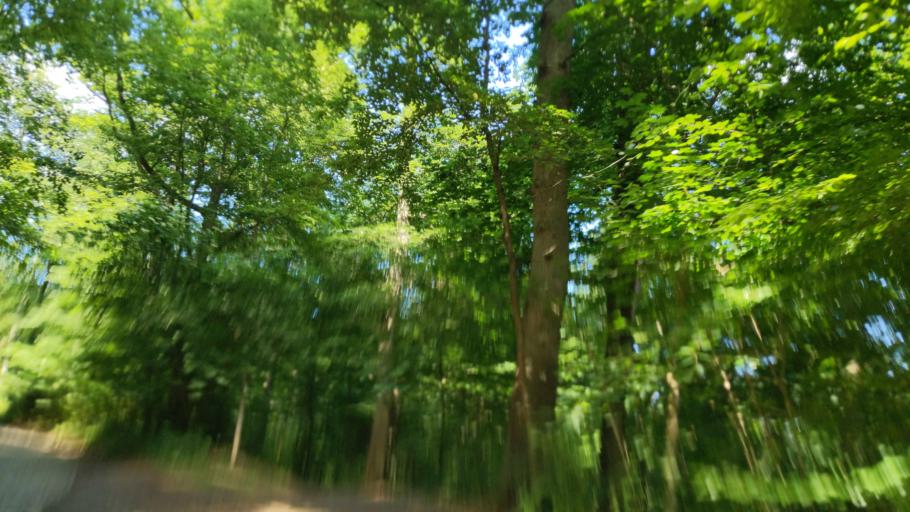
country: DE
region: Schleswig-Holstein
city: Schmilau
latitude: 53.6834
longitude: 10.7531
